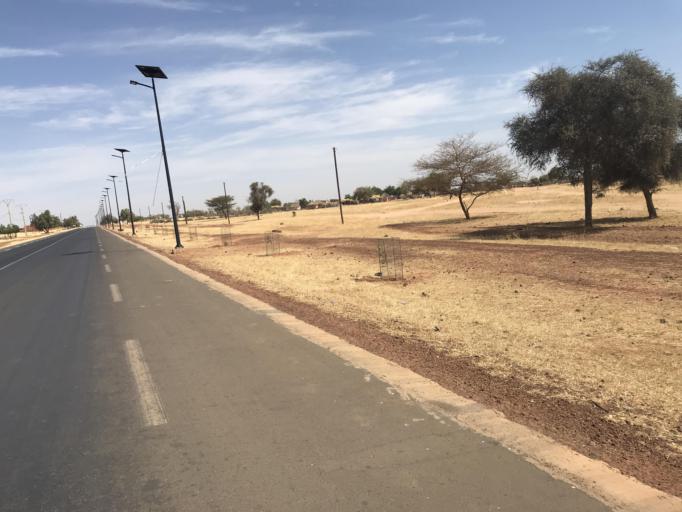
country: SN
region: Matam
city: Ranerou
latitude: 15.3009
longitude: -13.9551
